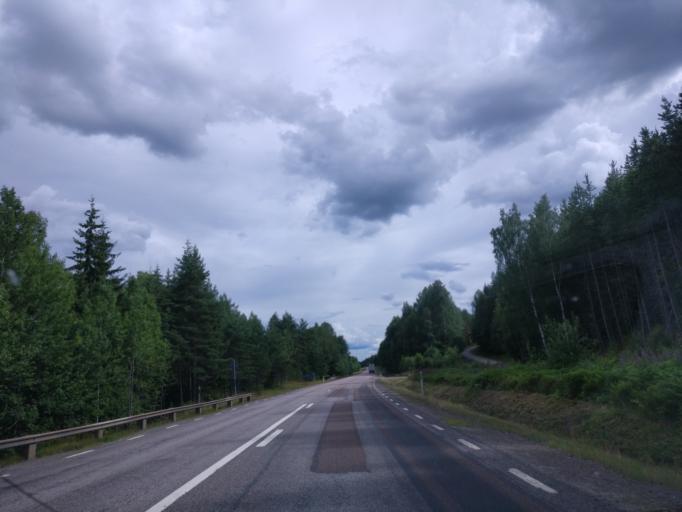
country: SE
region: Vaermland
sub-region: Hagfors Kommun
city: Ekshaerad
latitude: 60.1556
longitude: 13.5162
